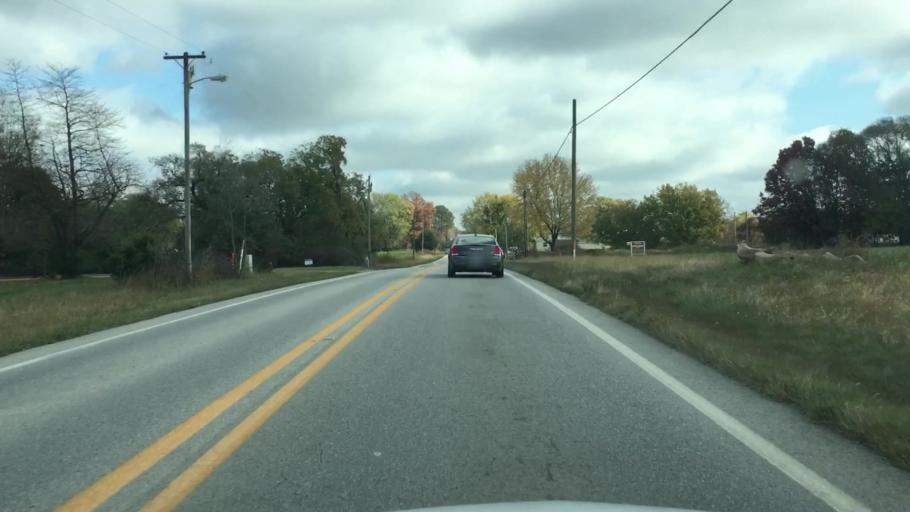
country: US
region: Arkansas
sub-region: Benton County
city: Gentry
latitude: 36.2639
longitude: -94.4781
